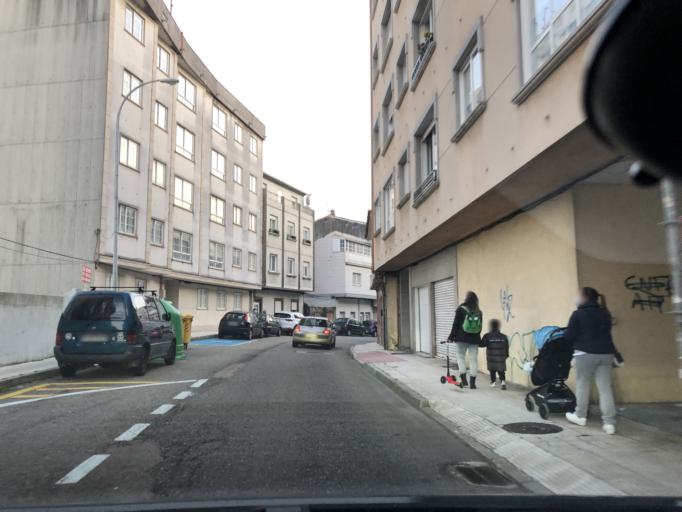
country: ES
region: Galicia
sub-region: Provincia de Pontevedra
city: Marin
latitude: 42.3929
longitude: -8.7063
